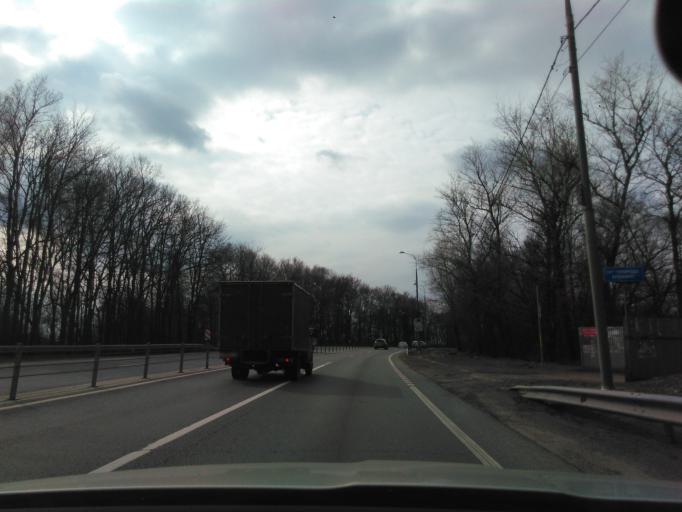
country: RU
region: Moskovskaya
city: Marfino
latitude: 56.0151
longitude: 37.5461
